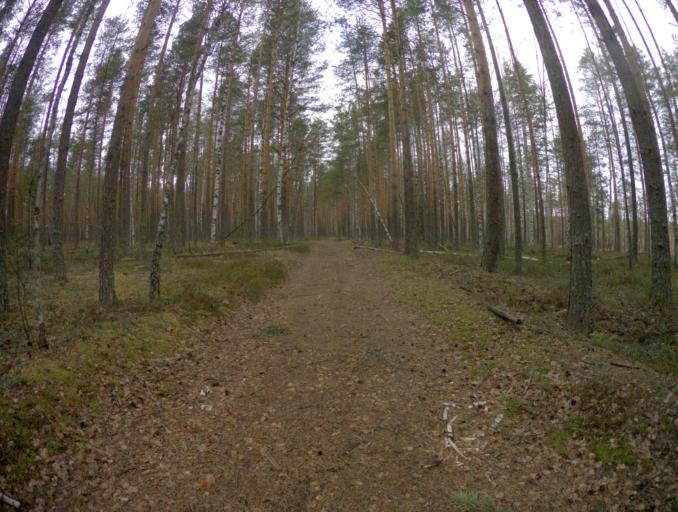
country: RU
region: Vladimir
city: Raduzhnyy
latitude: 55.9463
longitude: 40.2908
